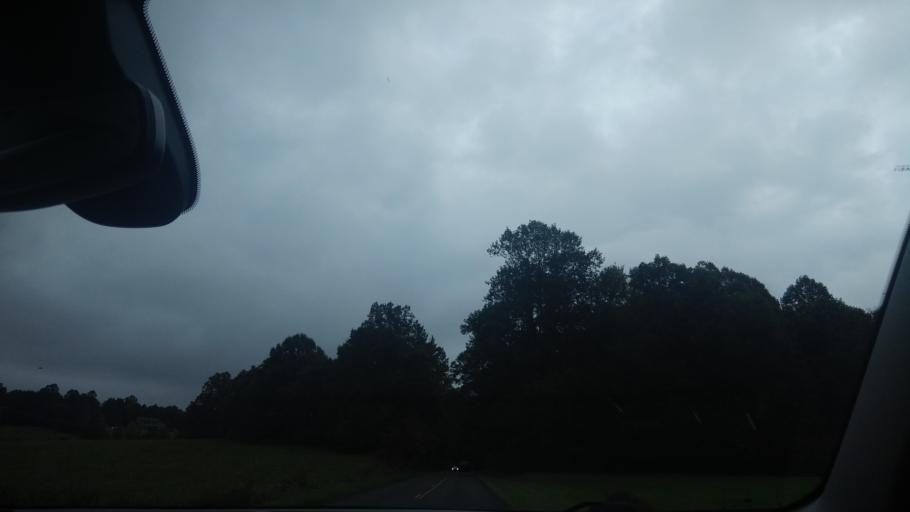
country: US
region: Virginia
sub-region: Carroll County
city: Cana
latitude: 36.6720
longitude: -80.6209
